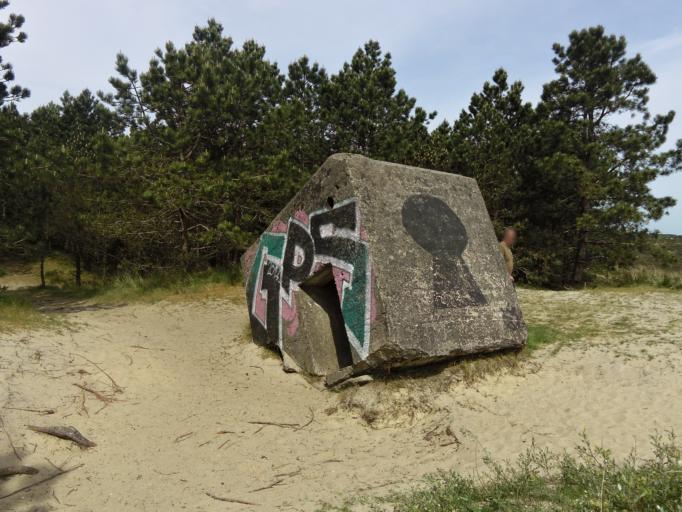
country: DE
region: Schleswig-Holstein
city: List
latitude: 55.1523
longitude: 8.5319
